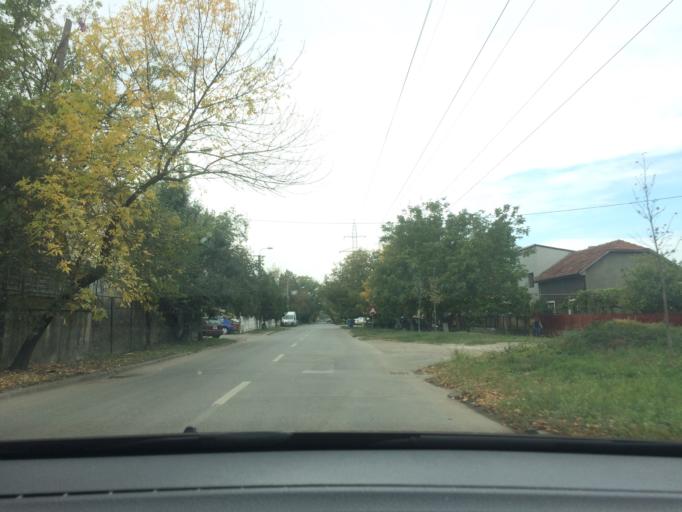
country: RO
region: Timis
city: Timisoara
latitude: 45.7516
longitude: 21.1946
